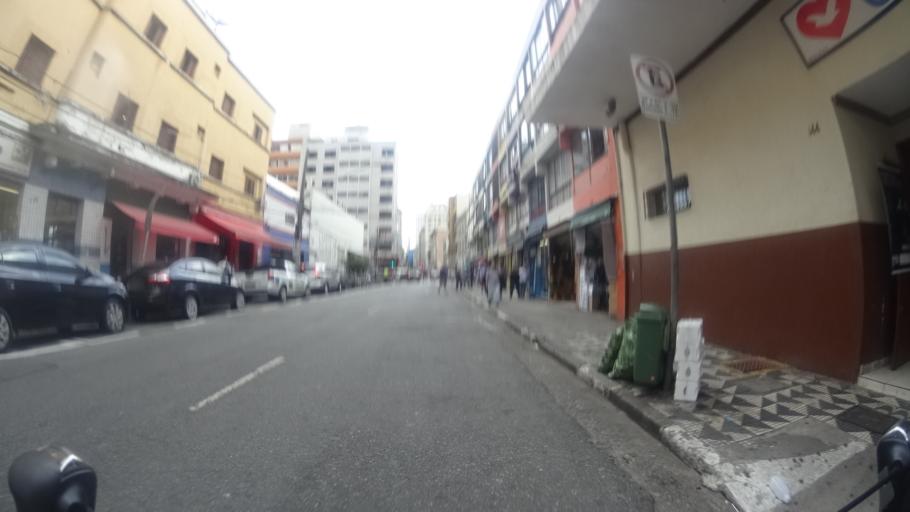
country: BR
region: Sao Paulo
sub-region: Sao Paulo
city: Sao Paulo
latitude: -23.5393
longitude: -46.6377
